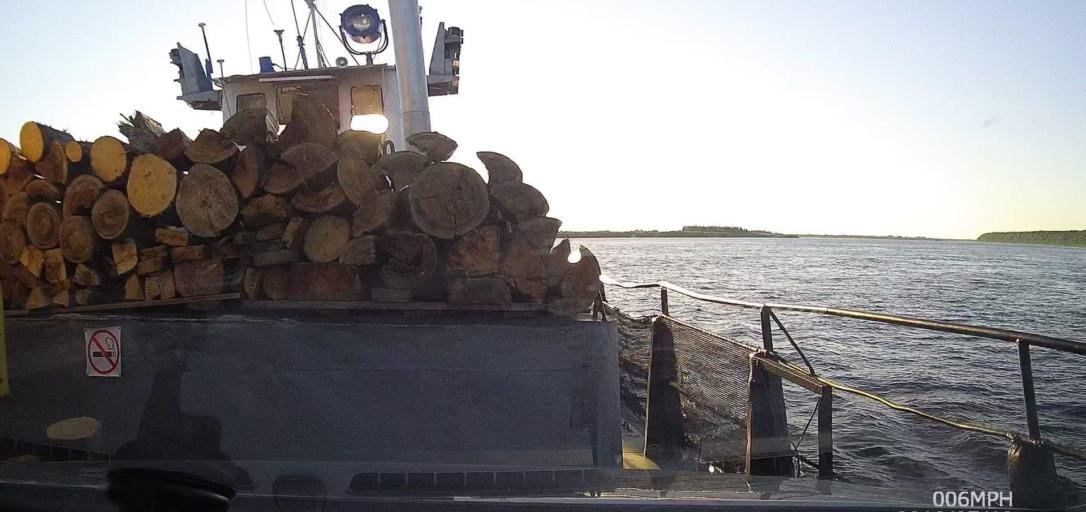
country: RU
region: Arkhangelskaya
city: Lukovetskiy
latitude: 64.1579
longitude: 41.9176
